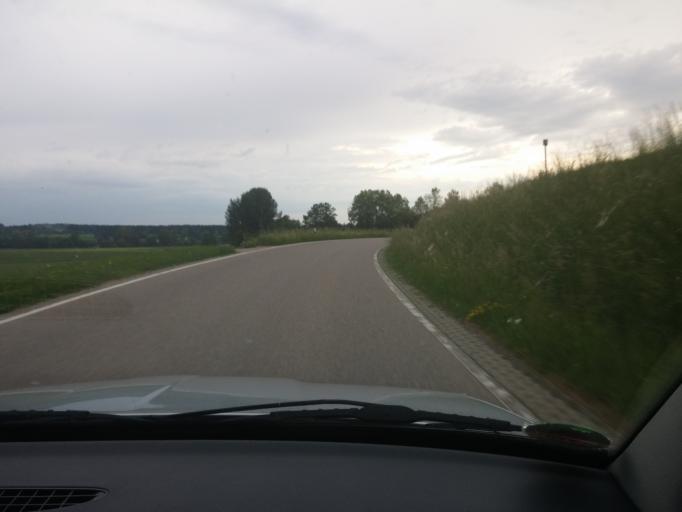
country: DE
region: Bavaria
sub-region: Swabia
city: Legau
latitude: 47.8323
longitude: 10.1026
